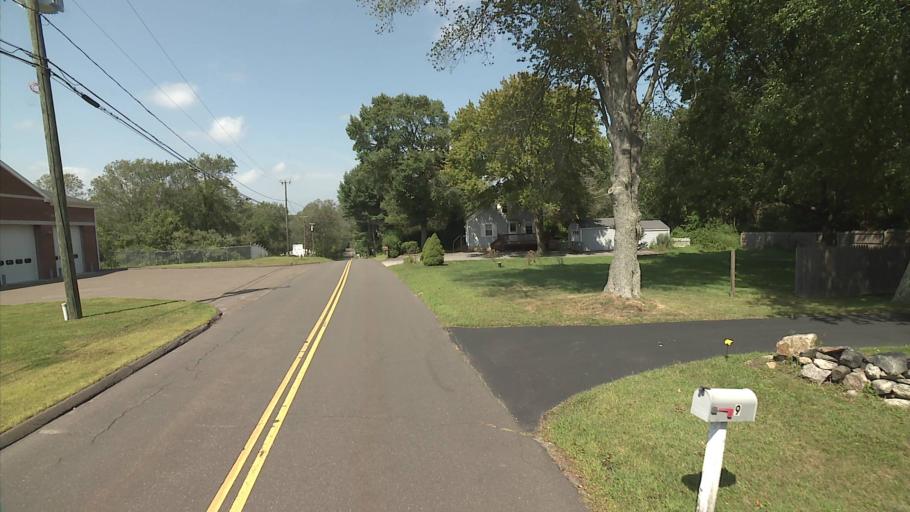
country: US
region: Connecticut
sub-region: New London County
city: Niantic
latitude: 41.3524
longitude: -72.2566
